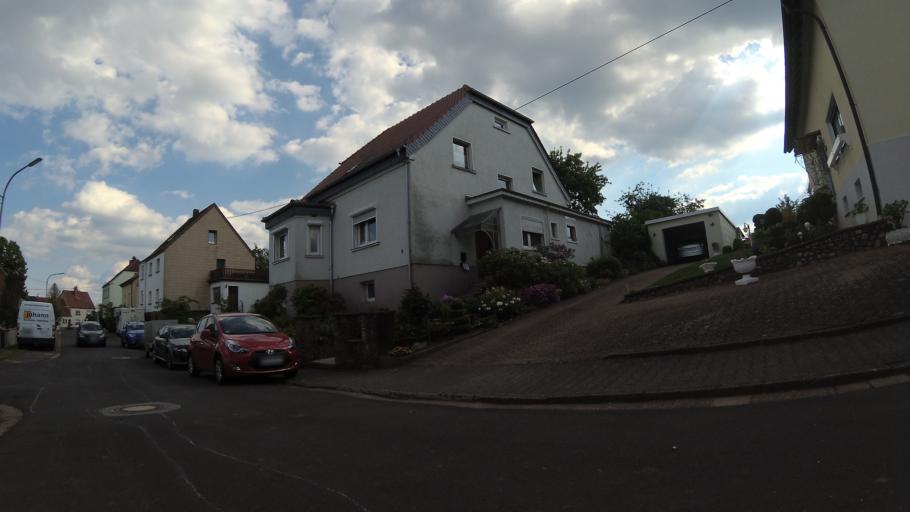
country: DE
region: Saarland
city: Oberthal
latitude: 49.5197
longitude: 7.1004
